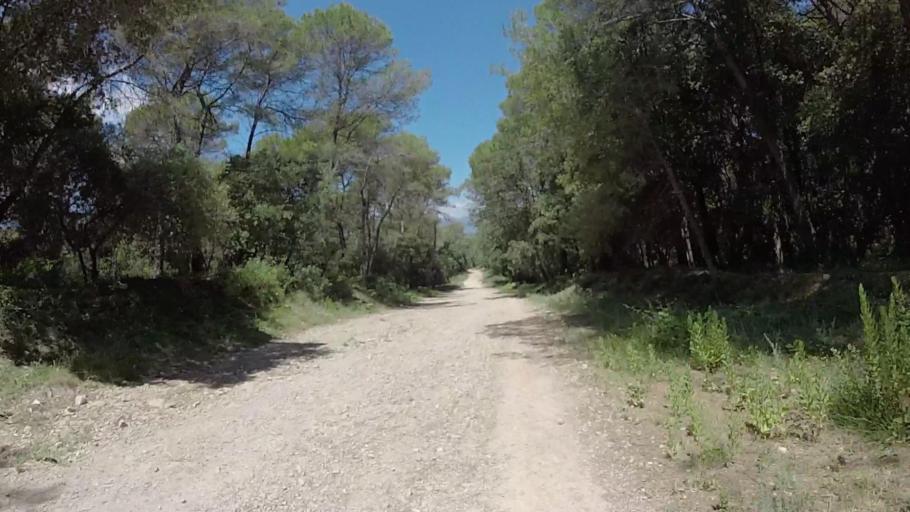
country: FR
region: Provence-Alpes-Cote d'Azur
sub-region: Departement des Alpes-Maritimes
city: Mougins
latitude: 43.5962
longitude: 7.0217
